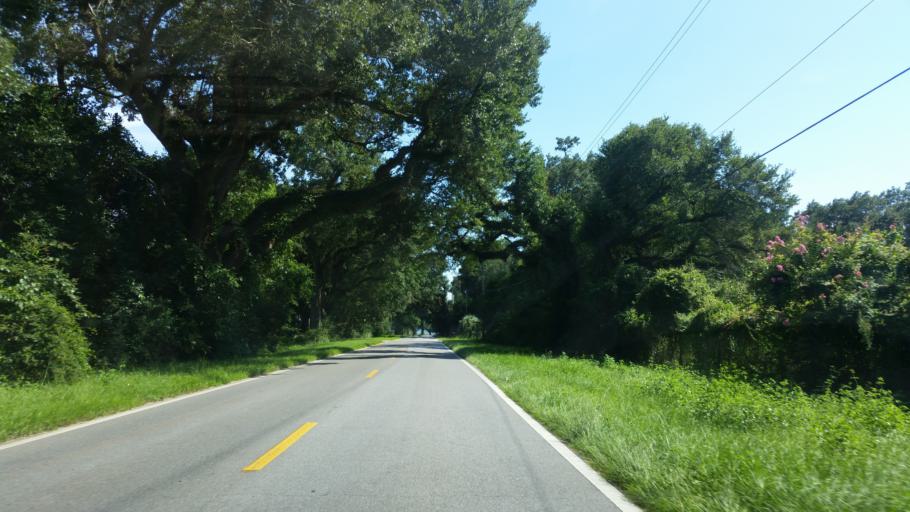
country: US
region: Florida
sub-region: Santa Rosa County
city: Pace
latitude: 30.5858
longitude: -87.1613
